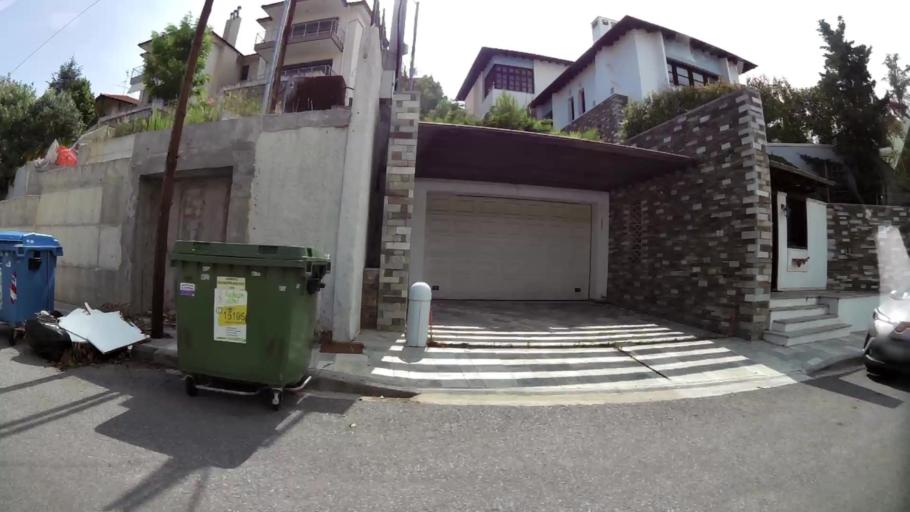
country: GR
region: Central Macedonia
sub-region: Nomos Thessalonikis
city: Panorama
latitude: 40.5795
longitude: 23.0194
